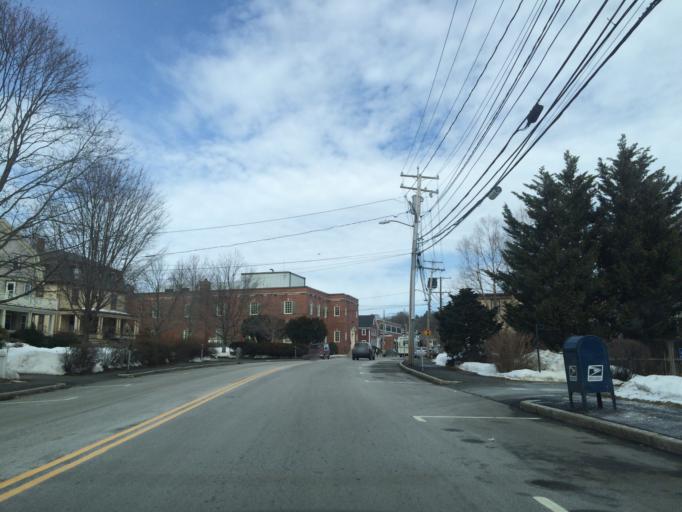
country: US
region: Massachusetts
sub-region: Middlesex County
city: Lexington
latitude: 42.4455
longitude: -71.2286
